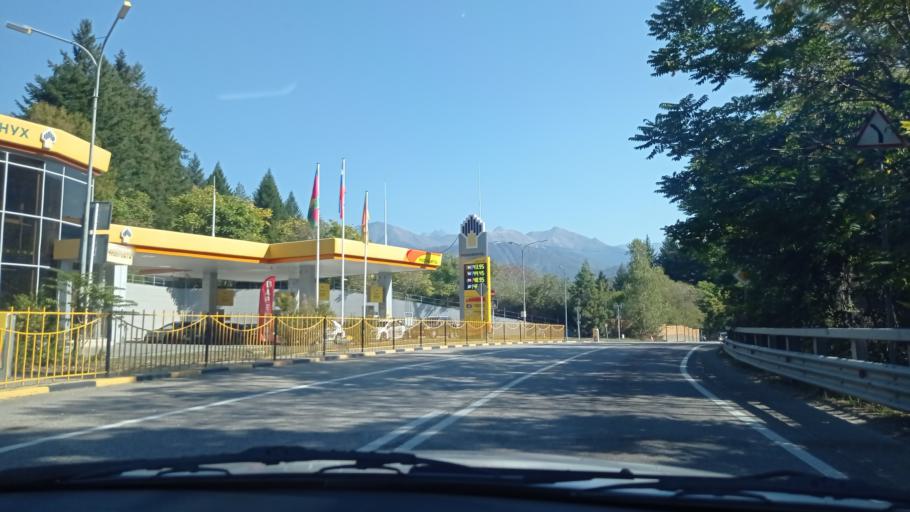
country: RU
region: Krasnodarskiy
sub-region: Sochi City
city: Krasnaya Polyana
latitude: 43.6825
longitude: 40.2205
